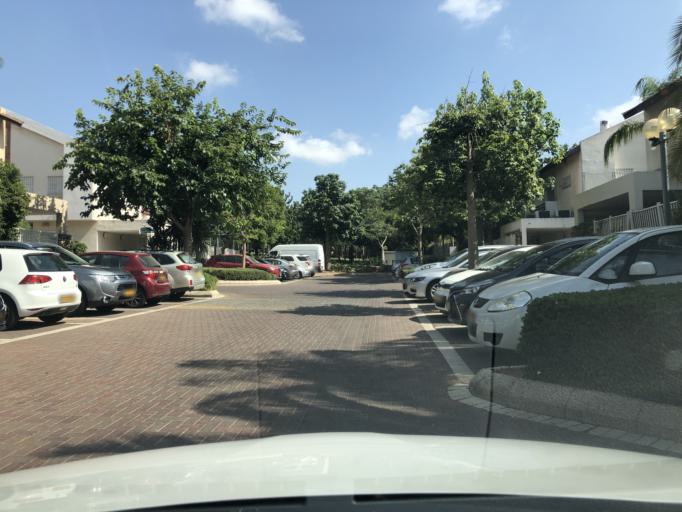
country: IL
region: Tel Aviv
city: Giv`at Shemu'el
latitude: 32.0643
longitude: 34.8469
